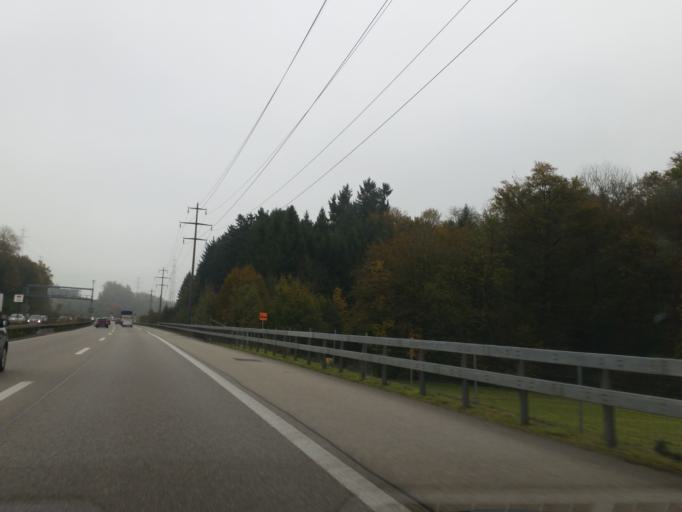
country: CH
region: Solothurn
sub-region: Bezirk Wasseramt
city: Deitingen
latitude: 47.2317
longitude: 7.6287
